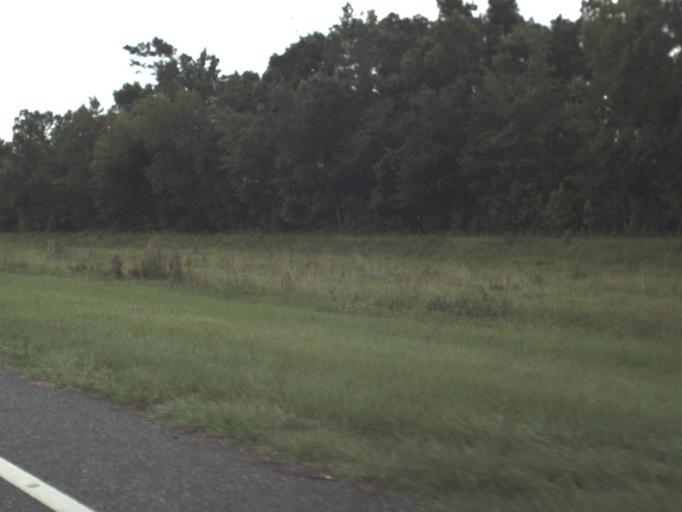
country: US
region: Florida
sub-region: Levy County
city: Inglis
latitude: 29.1933
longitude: -82.6865
